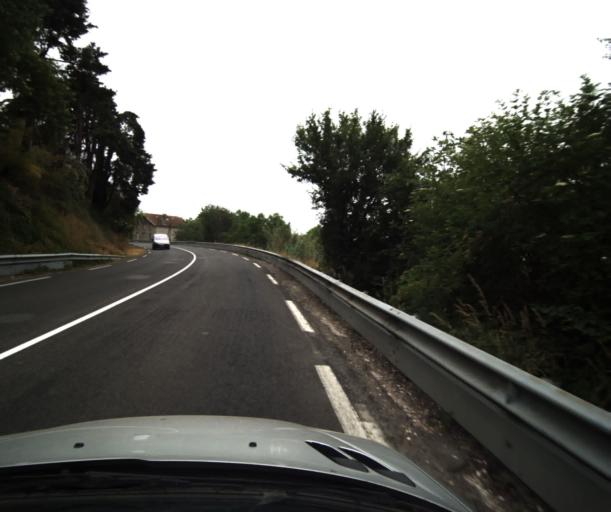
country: FR
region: Midi-Pyrenees
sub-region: Departement du Tarn-et-Garonne
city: Saint-Nicolas-de-la-Grave
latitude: 44.0920
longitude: 1.0386
